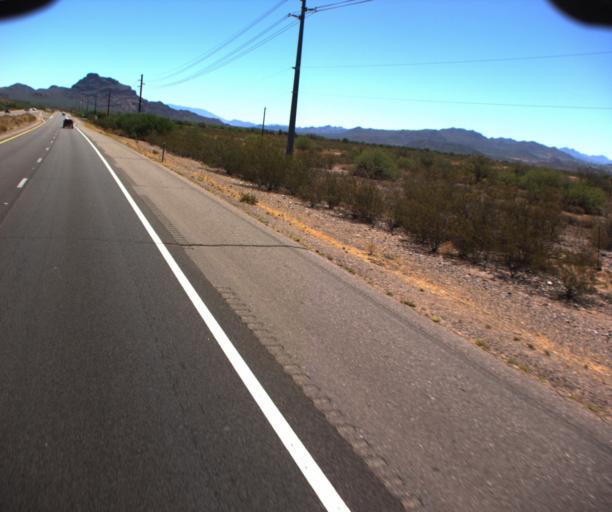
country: US
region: Arizona
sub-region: Maricopa County
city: Mesa
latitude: 33.5112
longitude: -111.7608
